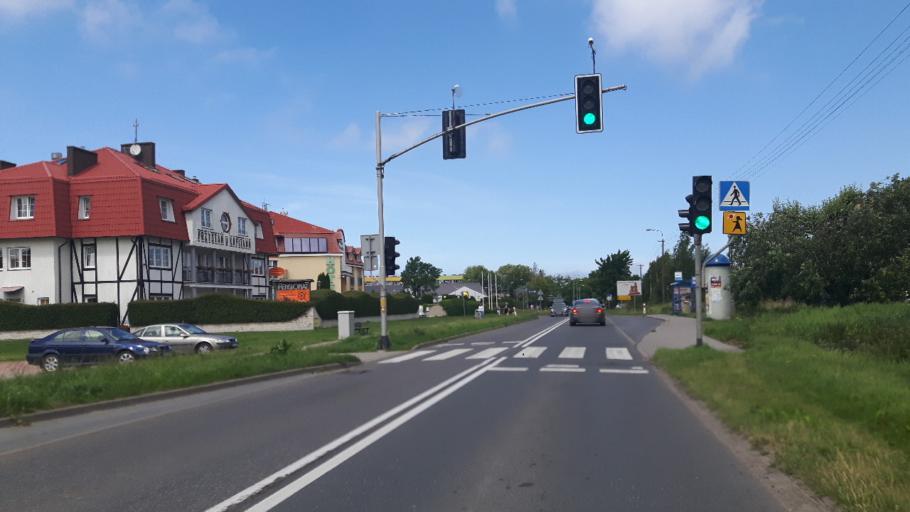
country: PL
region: Pomeranian Voivodeship
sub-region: Powiat slupski
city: Ustka
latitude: 54.5735
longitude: 16.8521
